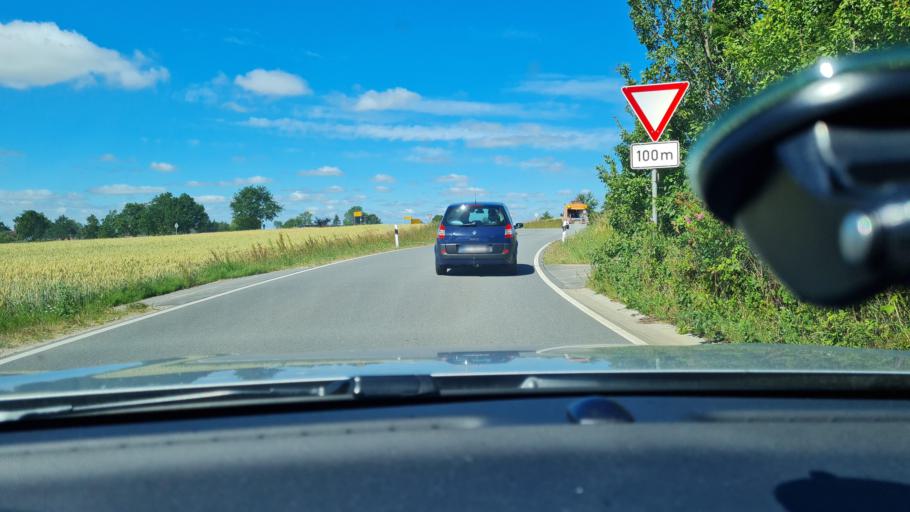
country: DE
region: Schleswig-Holstein
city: Rabel
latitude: 54.7236
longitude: 9.9540
